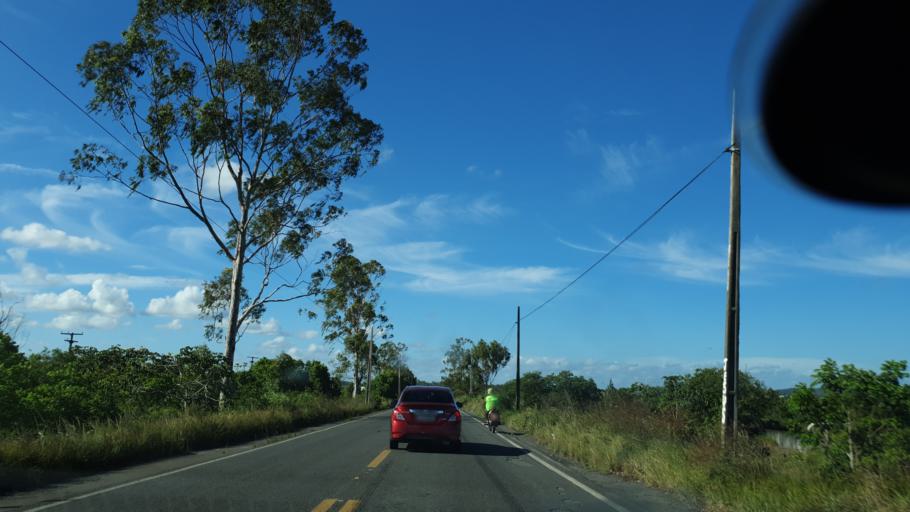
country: BR
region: Bahia
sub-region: Camacari
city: Camacari
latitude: -12.6539
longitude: -38.3030
